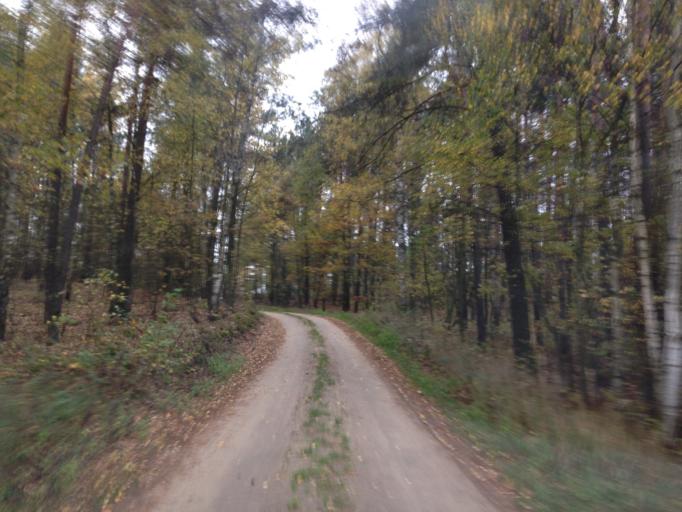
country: PL
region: Kujawsko-Pomorskie
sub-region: Powiat brodnicki
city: Bartniczka
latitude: 53.2743
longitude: 19.6772
